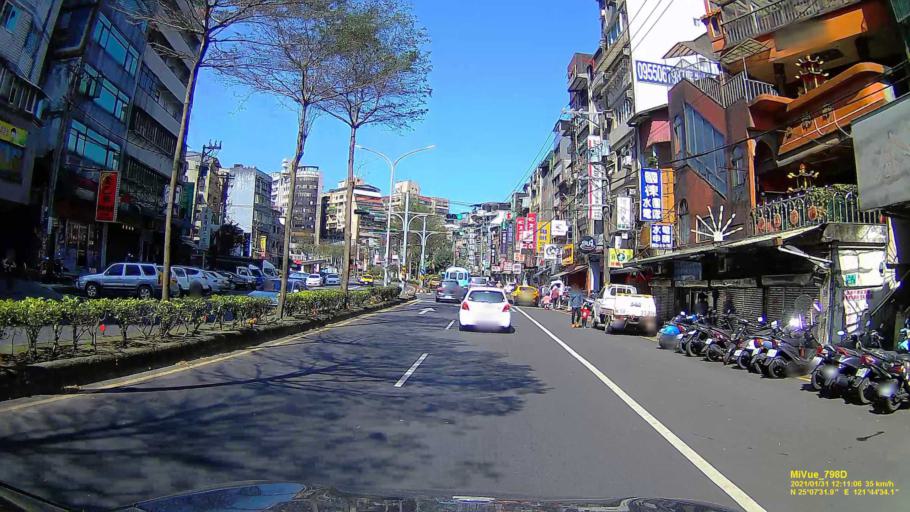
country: TW
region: Taiwan
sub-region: Keelung
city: Keelung
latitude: 25.1257
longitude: 121.7428
